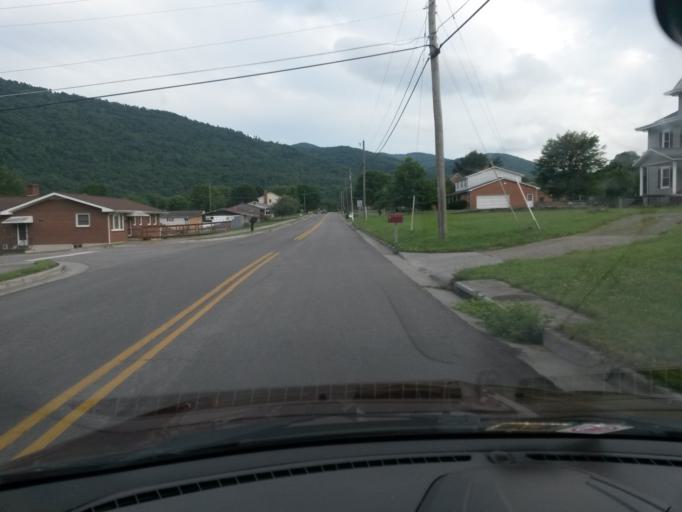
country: US
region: Virginia
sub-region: City of Covington
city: Fairlawn
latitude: 37.7670
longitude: -79.9702
